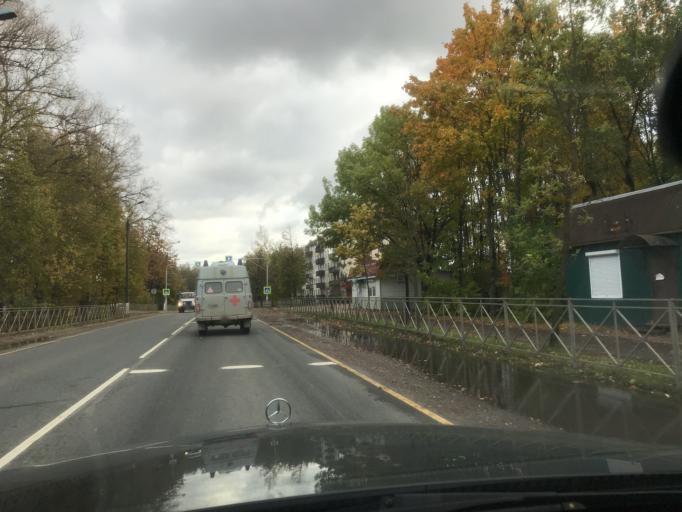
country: RU
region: Pskov
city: Pustoshka
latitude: 56.3345
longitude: 29.3704
